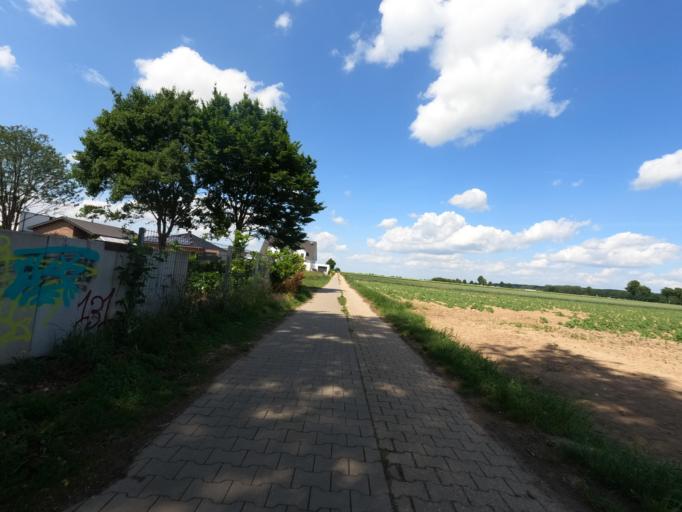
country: DE
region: North Rhine-Westphalia
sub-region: Regierungsbezirk Koln
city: Wassenberg
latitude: 51.0715
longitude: 6.1753
